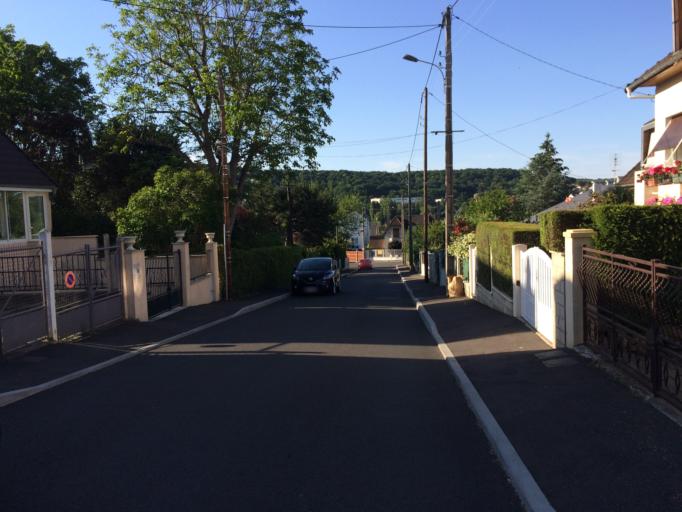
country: FR
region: Ile-de-France
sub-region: Departement de l'Essonne
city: Igny
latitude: 48.7316
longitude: 2.2192
